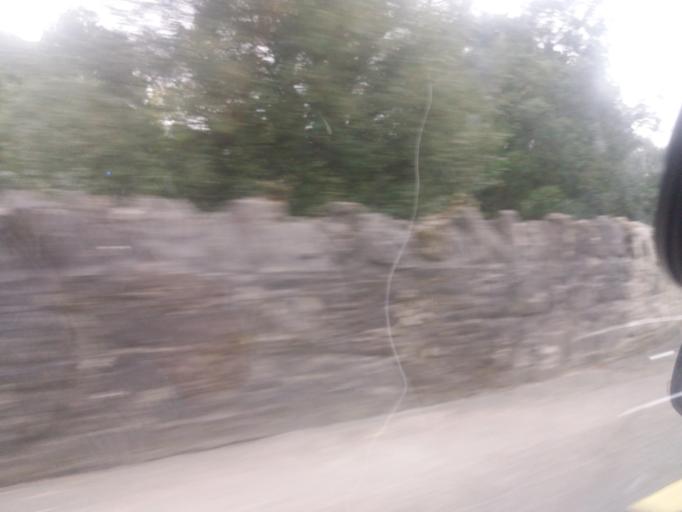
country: IE
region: Munster
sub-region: County Limerick
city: Adare
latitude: 52.5699
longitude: -8.7844
